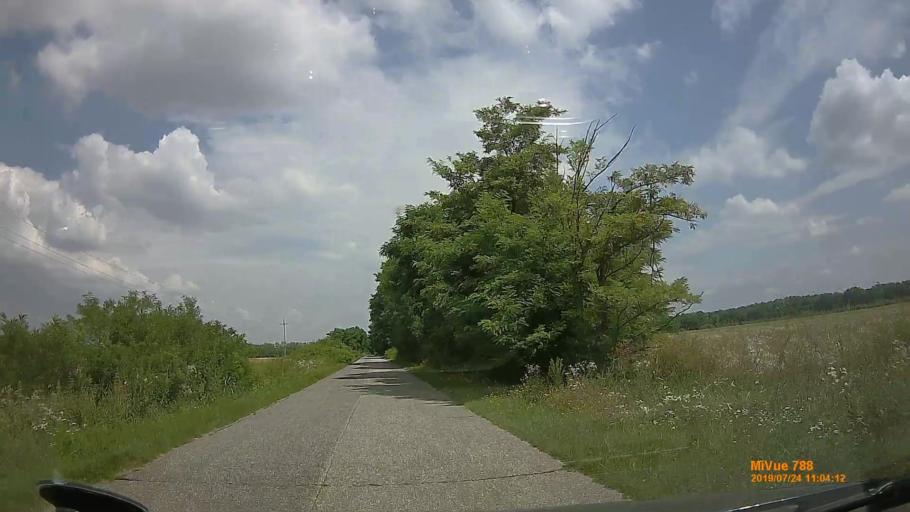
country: HU
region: Szabolcs-Szatmar-Bereg
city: Tarpa
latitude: 48.1672
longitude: 22.5162
